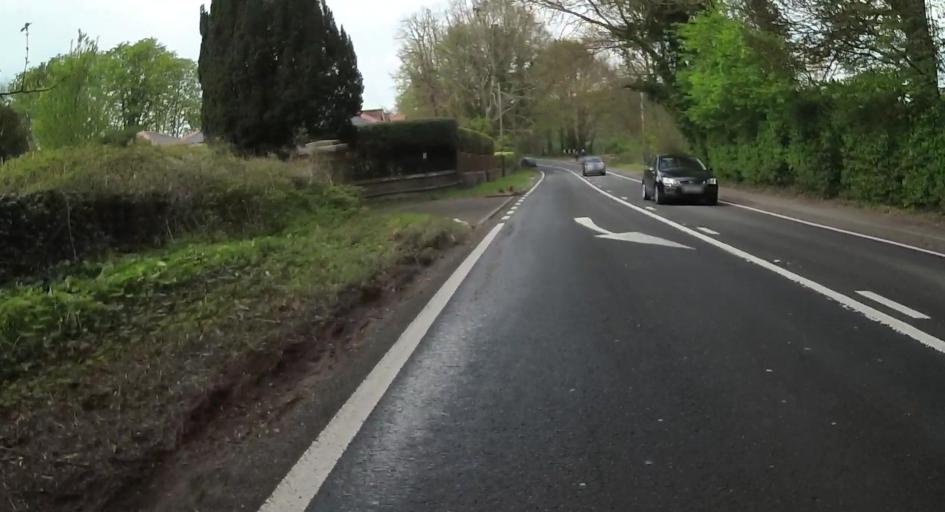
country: GB
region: England
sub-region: Hampshire
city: Compton
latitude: 51.0264
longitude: -1.3130
